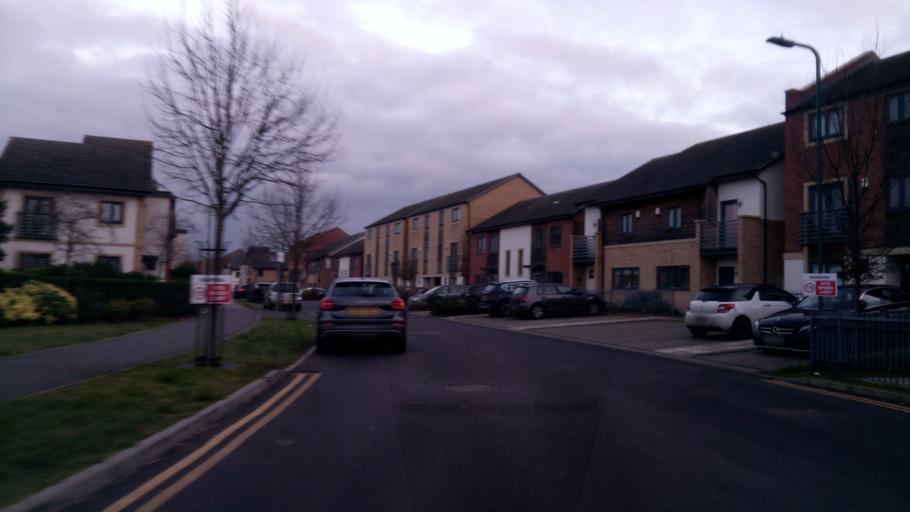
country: GB
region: England
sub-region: Peterborough
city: Peterborough
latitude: 52.5657
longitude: -0.2396
